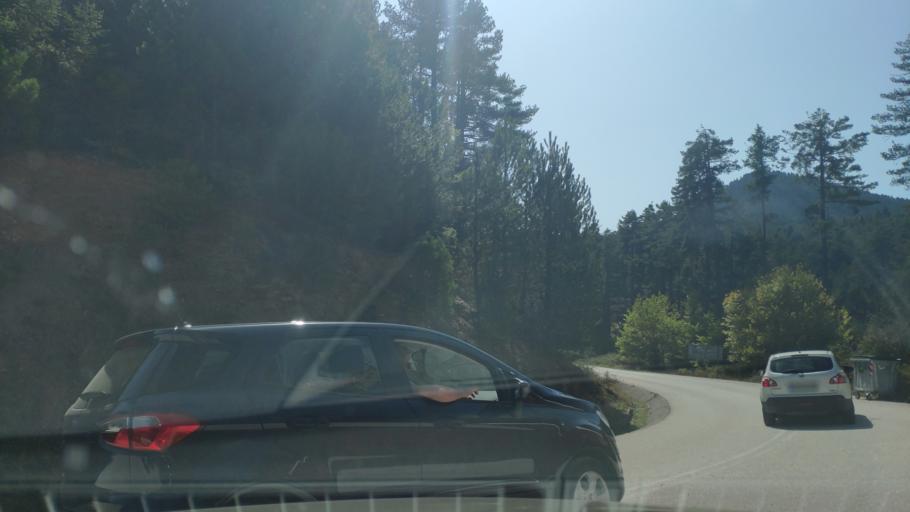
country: GR
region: West Greece
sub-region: Nomos Achaias
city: Kalavryta
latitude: 37.9274
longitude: 22.2861
